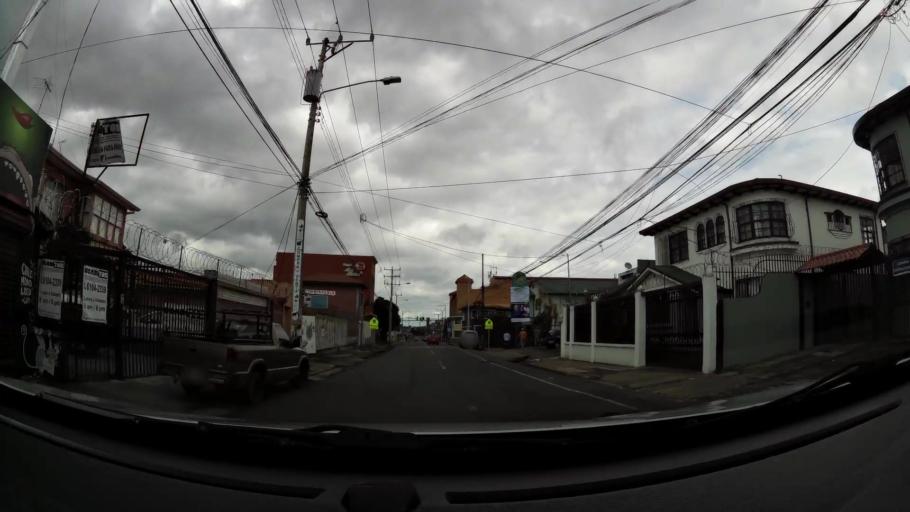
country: CR
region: San Jose
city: San Pedro
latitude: 9.9310
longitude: -84.0511
